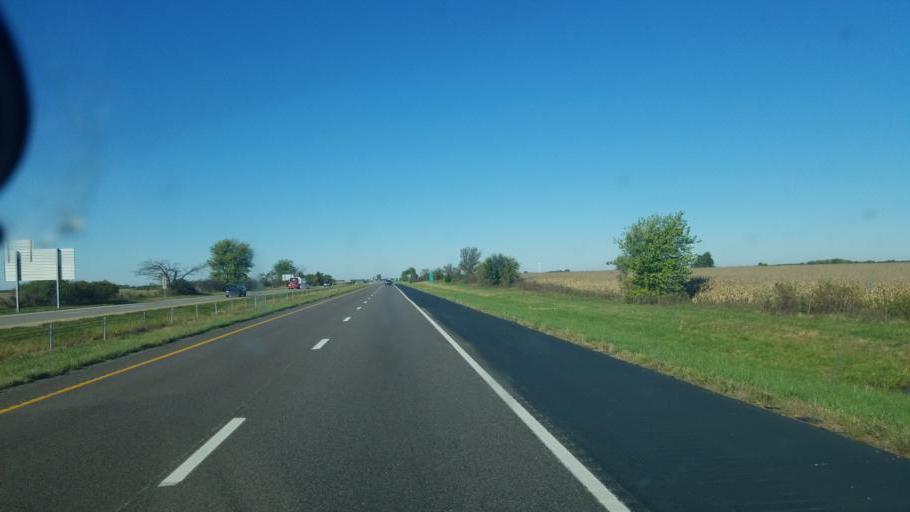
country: US
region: Missouri
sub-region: Montgomery County
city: Wellsville
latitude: 38.9116
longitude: -91.7069
